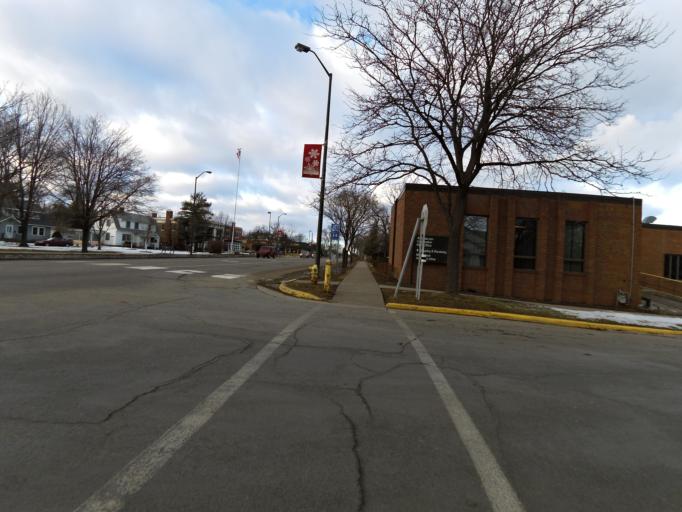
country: US
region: Minnesota
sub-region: Washington County
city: Bayport
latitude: 45.0207
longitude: -92.7805
